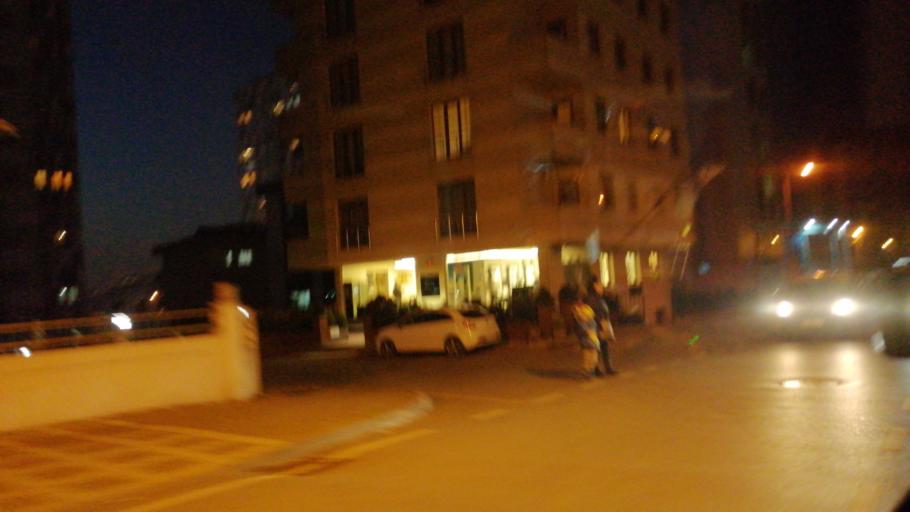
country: TR
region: Istanbul
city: Umraniye
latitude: 40.9981
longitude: 29.1422
